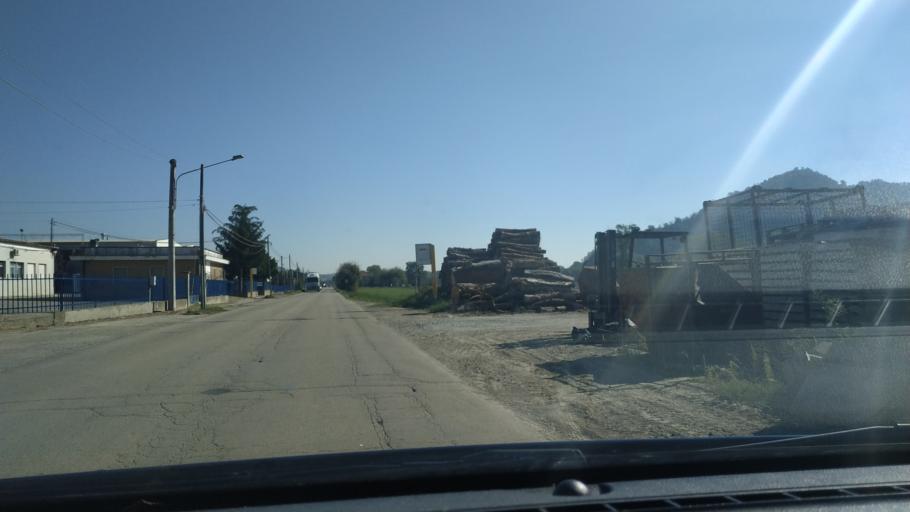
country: IT
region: Piedmont
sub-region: Provincia di Alessandria
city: Cerrina
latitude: 45.1162
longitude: 8.2187
